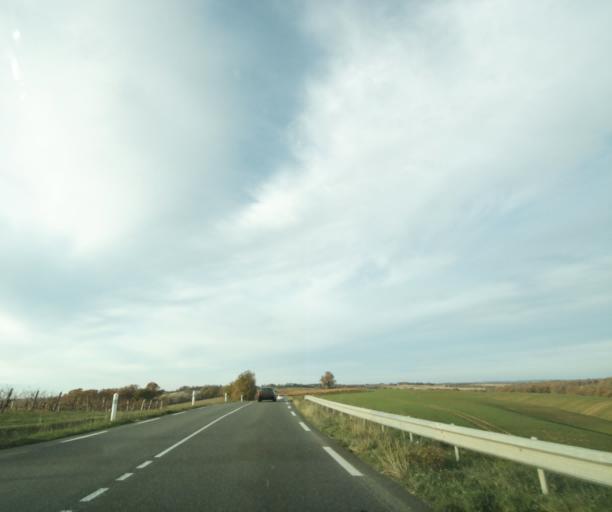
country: FR
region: Midi-Pyrenees
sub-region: Departement du Gers
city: Eauze
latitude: 43.7805
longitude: 0.1169
